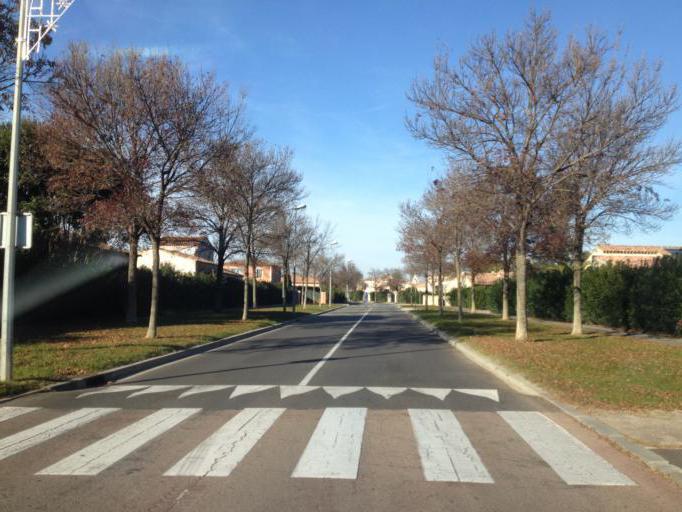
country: FR
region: Provence-Alpes-Cote d'Azur
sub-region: Departement des Bouches-du-Rhone
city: Istres
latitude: 43.5040
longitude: 4.9701
